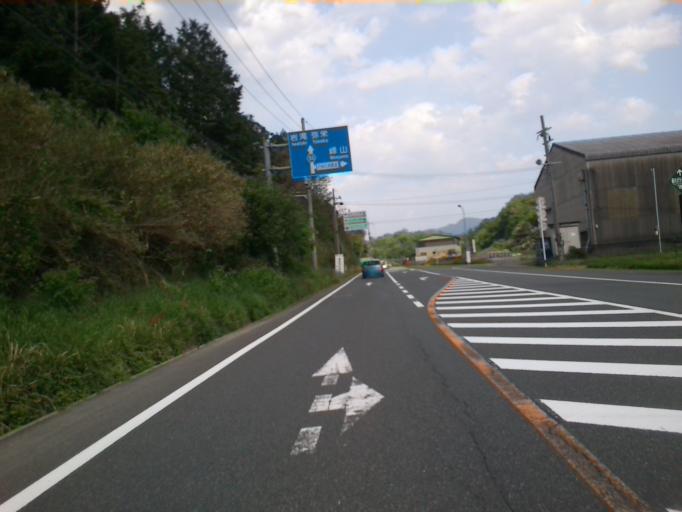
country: JP
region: Kyoto
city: Miyazu
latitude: 35.6846
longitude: 135.0598
